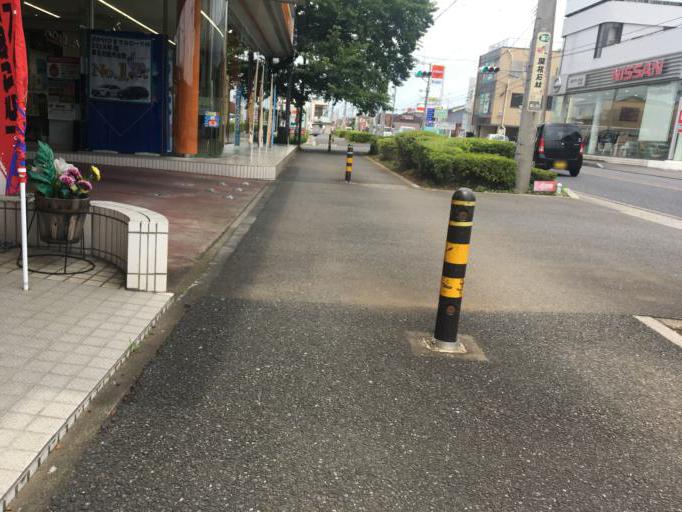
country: JP
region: Saitama
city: Kasukabe
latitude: 35.9754
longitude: 139.7650
